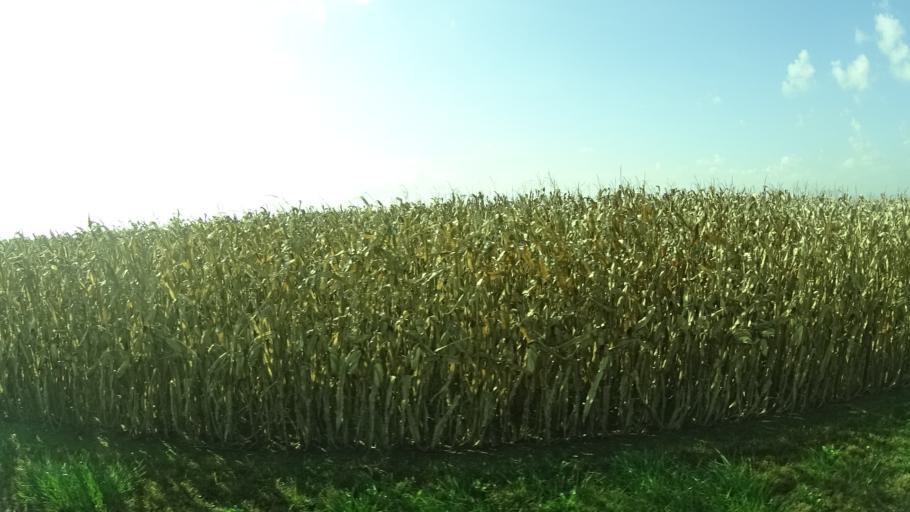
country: US
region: Indiana
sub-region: Madison County
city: Lapel
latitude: 40.0458
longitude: -85.8169
